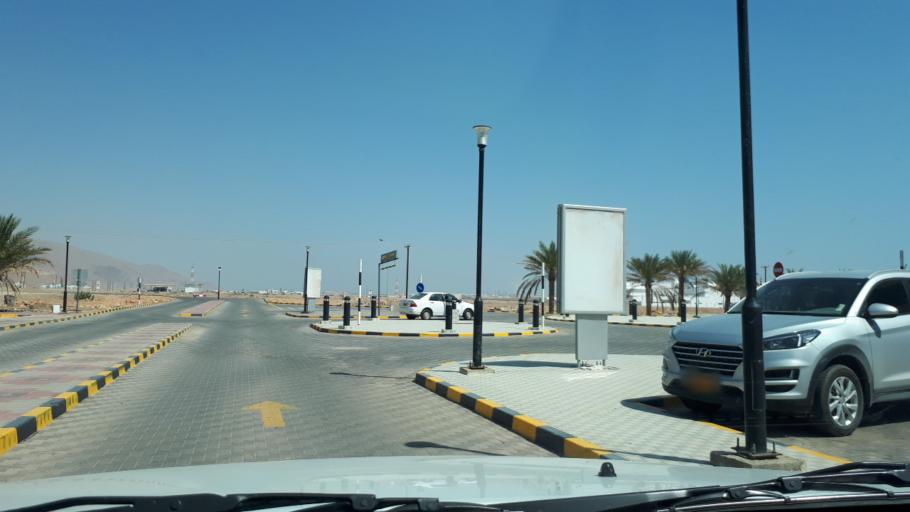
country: OM
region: Ash Sharqiyah
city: Sur
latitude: 22.5965
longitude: 59.4371
